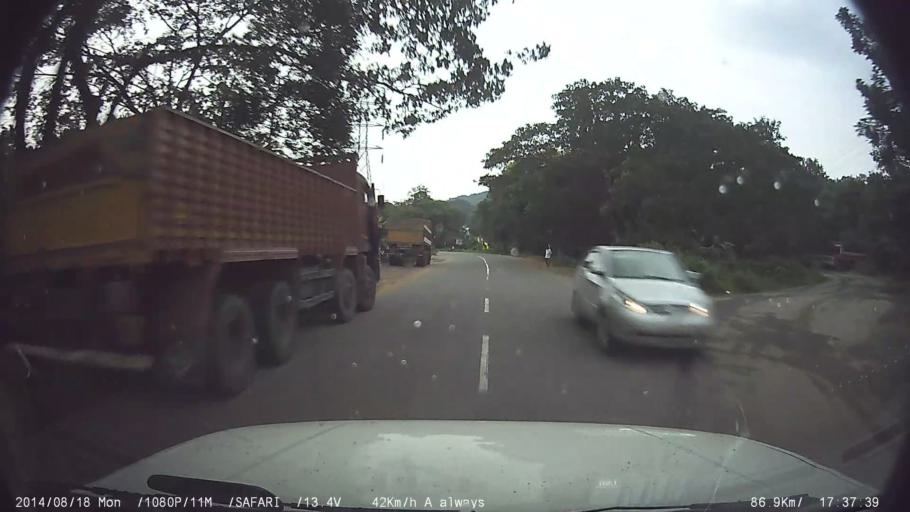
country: IN
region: Kerala
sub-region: Ernakulam
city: Muvattupuzha
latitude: 9.9107
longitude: 76.5836
